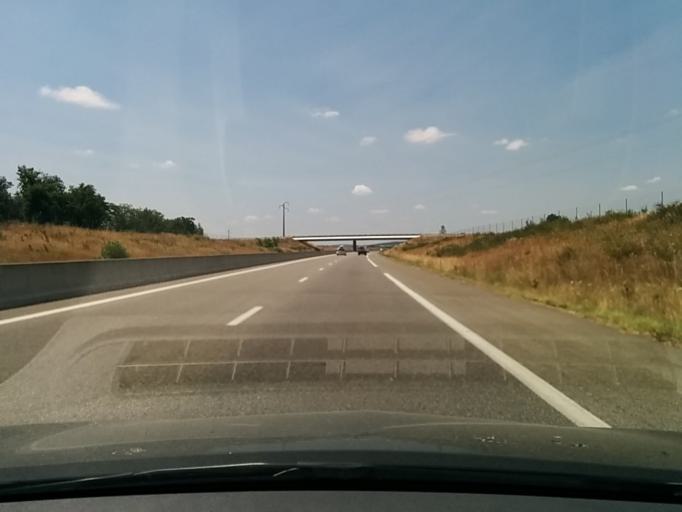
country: FR
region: Midi-Pyrenees
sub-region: Departement de la Haute-Garonne
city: Leguevin
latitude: 43.5820
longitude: 1.2397
